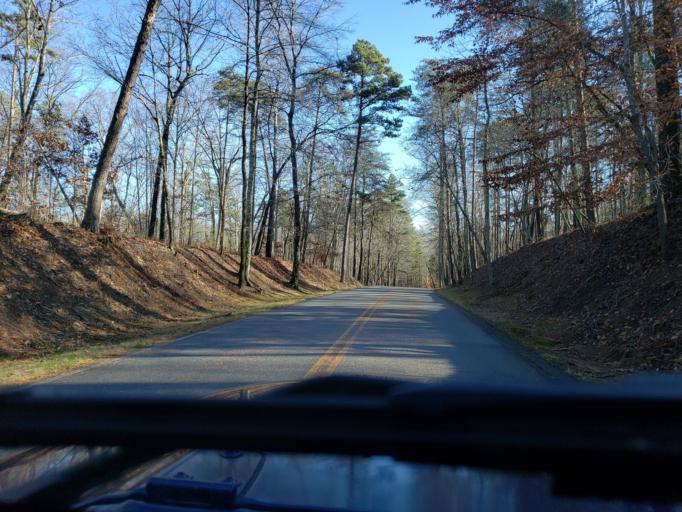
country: US
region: North Carolina
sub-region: Cleveland County
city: White Plains
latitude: 35.1516
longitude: -81.3938
